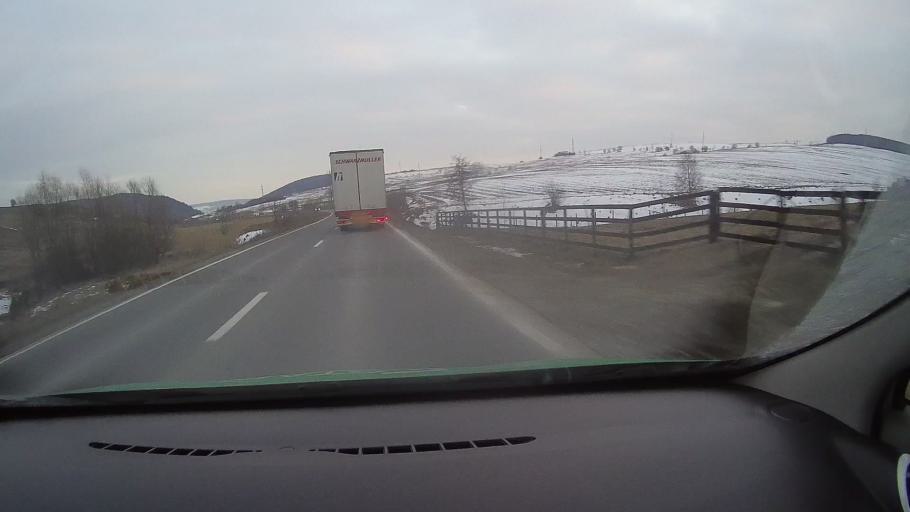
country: RO
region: Harghita
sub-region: Comuna Lupeni
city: Lupeni
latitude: 46.3483
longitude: 25.2637
